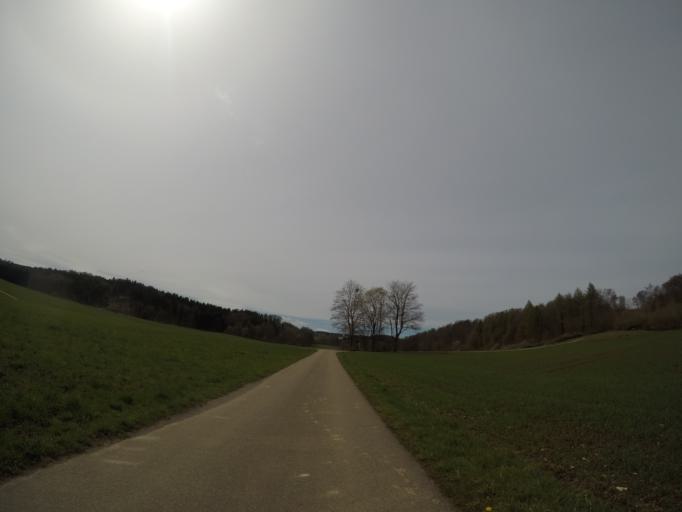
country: DE
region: Baden-Wuerttemberg
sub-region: Regierungsbezirk Stuttgart
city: Neidlingen
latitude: 48.5378
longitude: 9.5549
